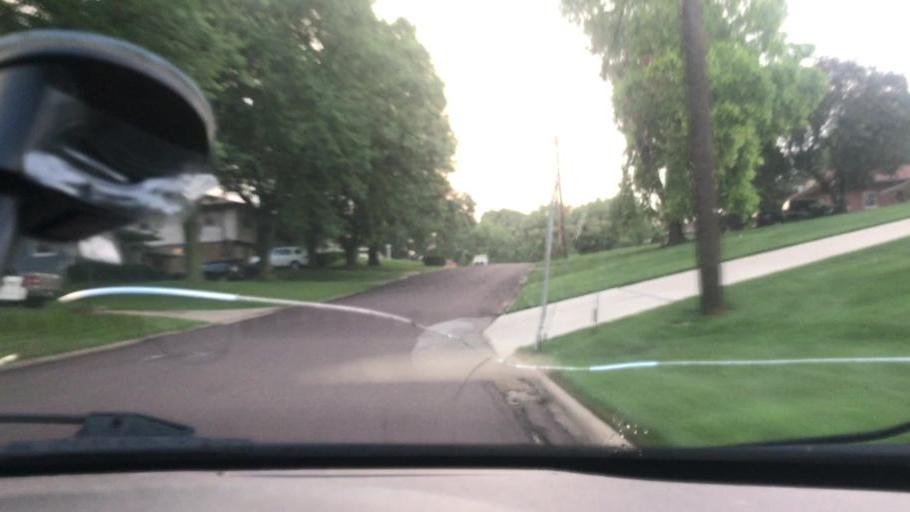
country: US
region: Illinois
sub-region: Tazewell County
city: Pekin
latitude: 40.5517
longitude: -89.6136
